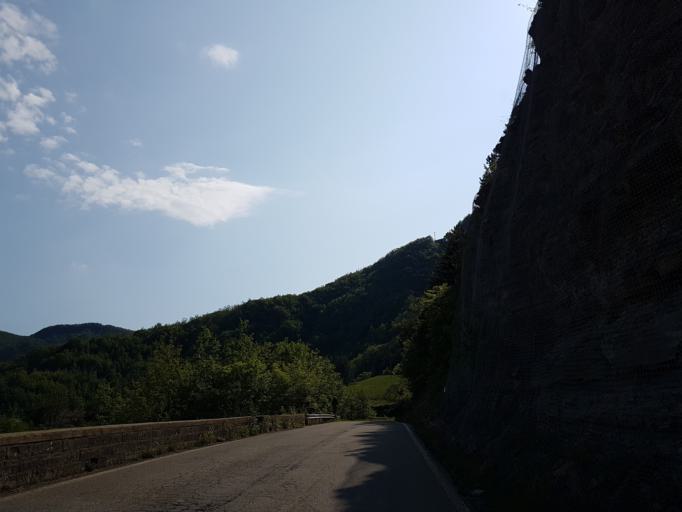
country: IT
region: Emilia-Romagna
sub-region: Forli-Cesena
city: San Piero in Bagno
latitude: 43.8113
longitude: 11.9268
